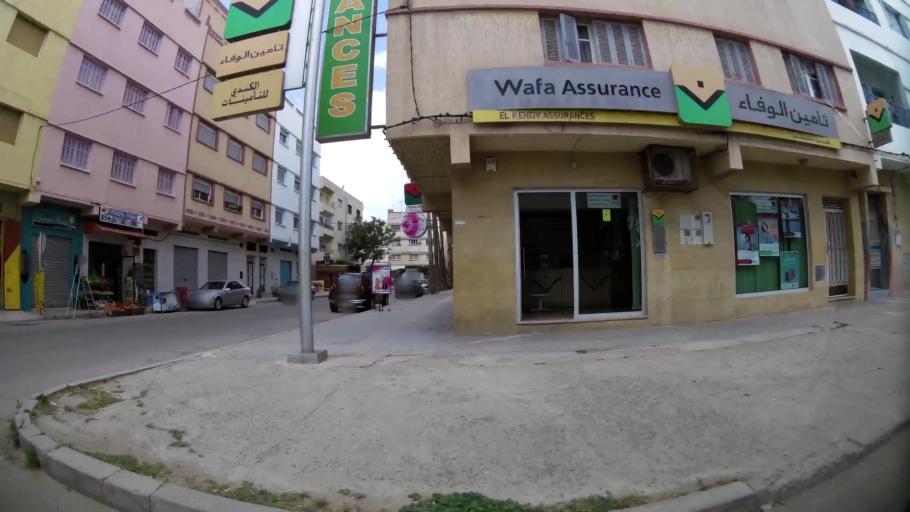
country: MA
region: Oriental
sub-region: Nador
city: Nador
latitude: 35.1689
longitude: -2.9277
